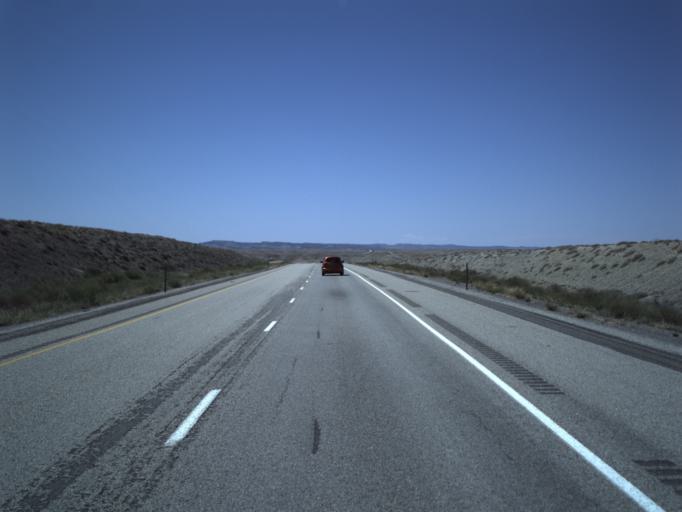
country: US
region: Utah
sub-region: Grand County
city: Moab
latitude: 38.9935
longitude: -109.3314
